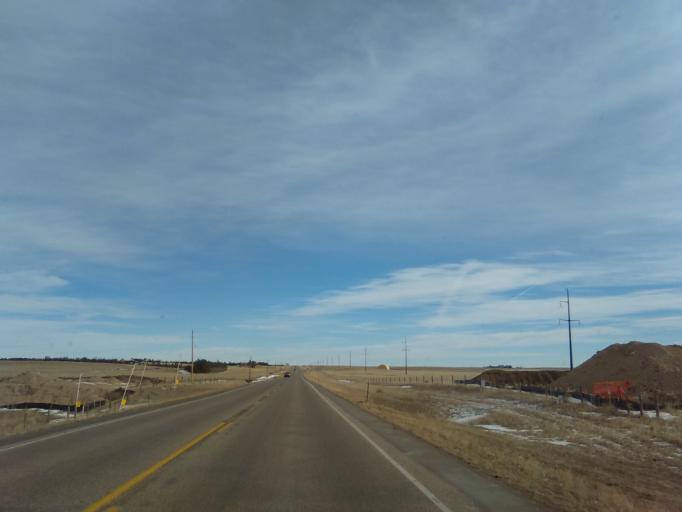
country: US
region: Wyoming
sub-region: Laramie County
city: Pine Bluffs
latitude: 41.4165
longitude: -104.4174
